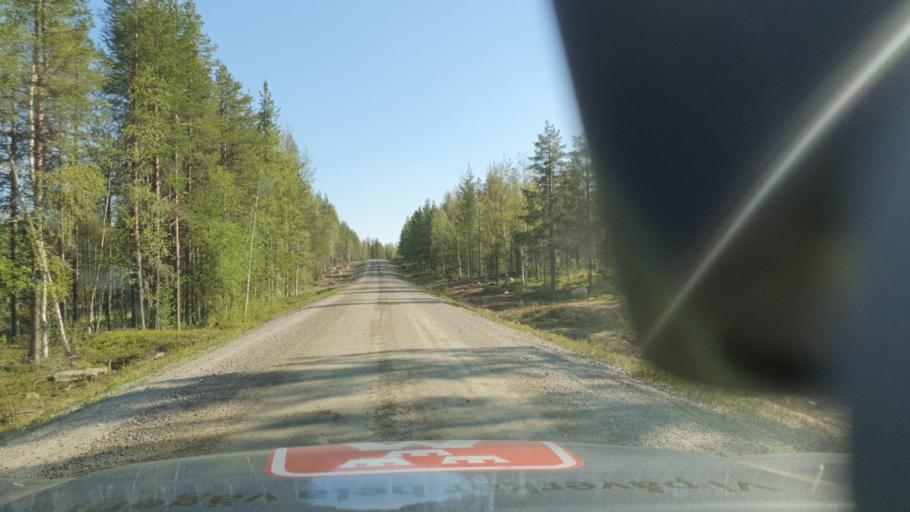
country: SE
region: Norrbotten
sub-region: Bodens Kommun
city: Boden
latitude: 66.4587
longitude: 21.8673
